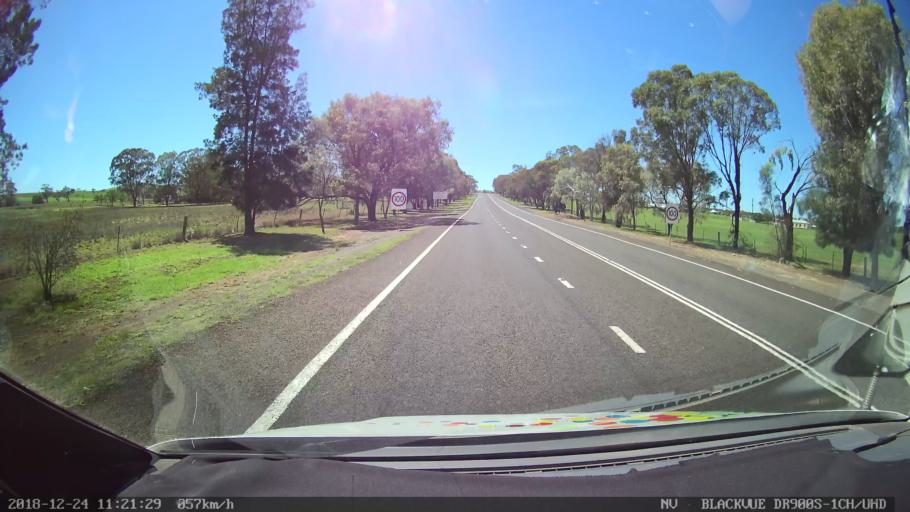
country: AU
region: New South Wales
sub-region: Upper Hunter Shire
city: Merriwa
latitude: -32.1433
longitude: 150.3706
